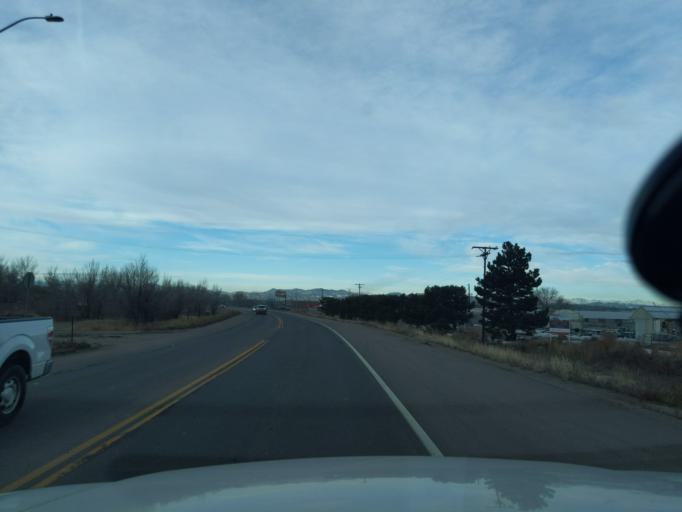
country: US
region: Colorado
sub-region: Adams County
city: Welby
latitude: 39.8308
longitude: -104.9503
